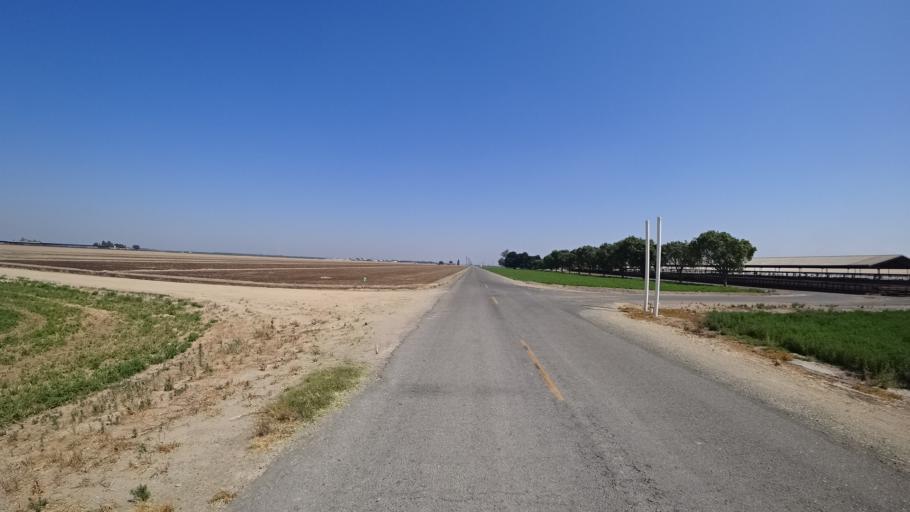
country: US
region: California
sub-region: Tulare County
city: Goshen
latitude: 36.3940
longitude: -119.5289
